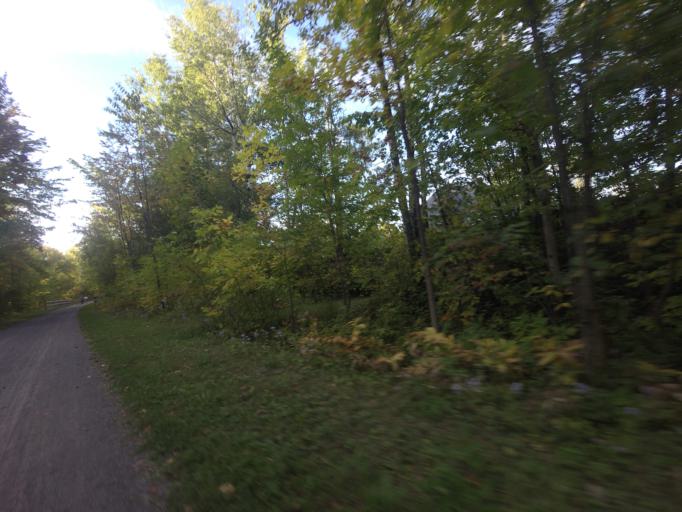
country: CA
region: Quebec
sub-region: Laurentides
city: Saint-Jerome
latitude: 45.8172
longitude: -74.0485
